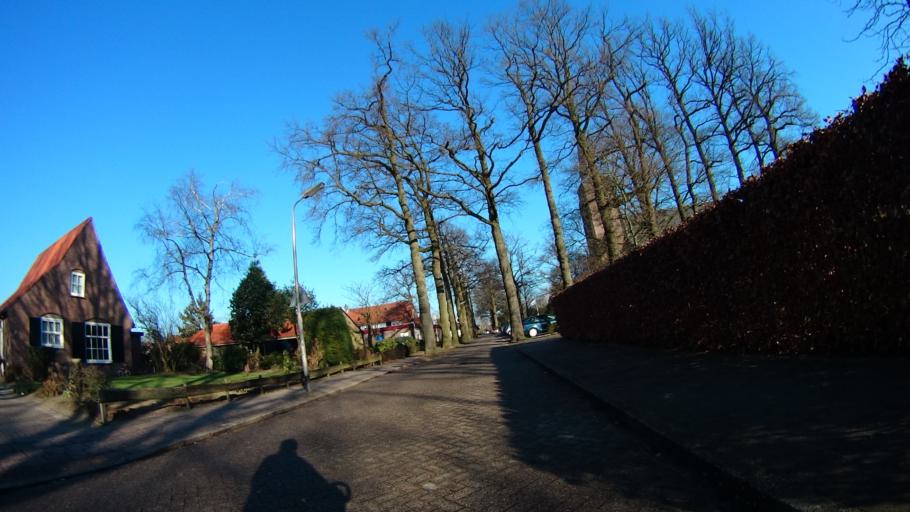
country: NL
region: Utrecht
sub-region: Gemeente Amersfoort
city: Hoogland
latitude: 52.1895
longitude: 5.3830
